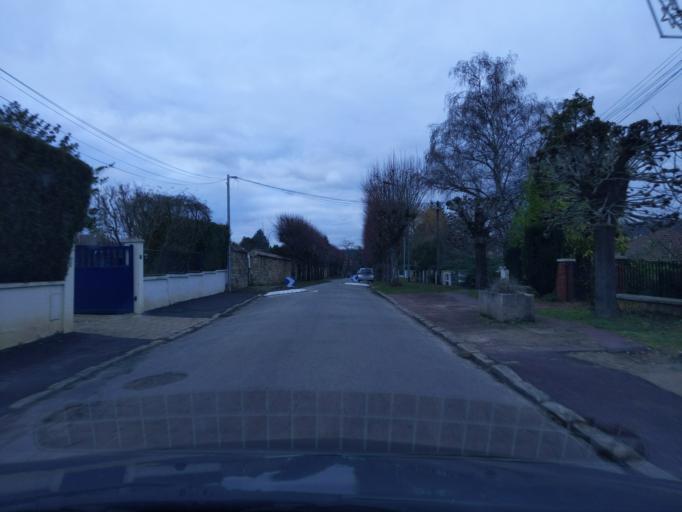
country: FR
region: Ile-de-France
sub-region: Departement des Yvelines
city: Saint-Remy-les-Chevreuse
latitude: 48.7085
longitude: 2.0657
